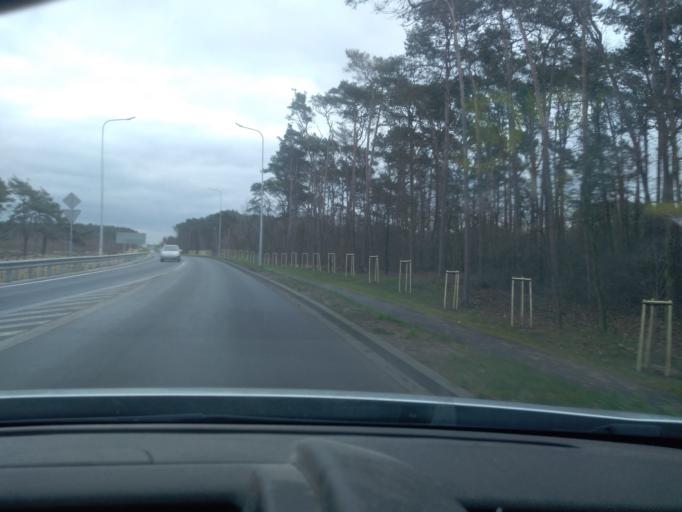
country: PL
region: Greater Poland Voivodeship
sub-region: Powiat obornicki
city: Oborniki
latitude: 52.6544
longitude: 16.8063
